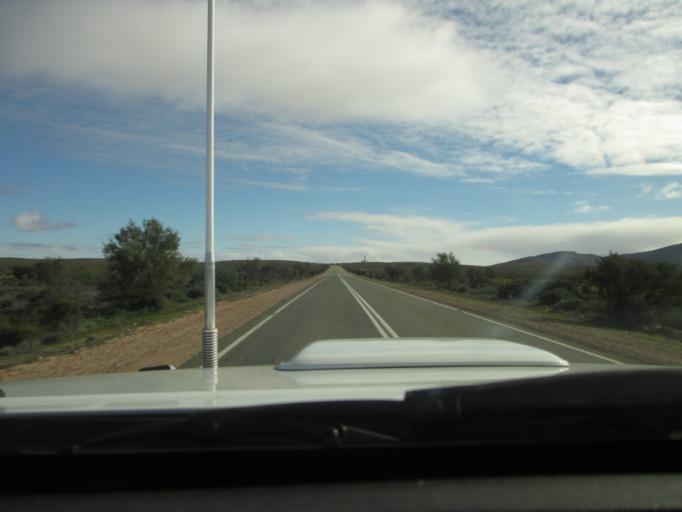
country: AU
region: South Australia
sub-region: Flinders Ranges
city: Quorn
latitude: -31.8196
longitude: 138.3771
